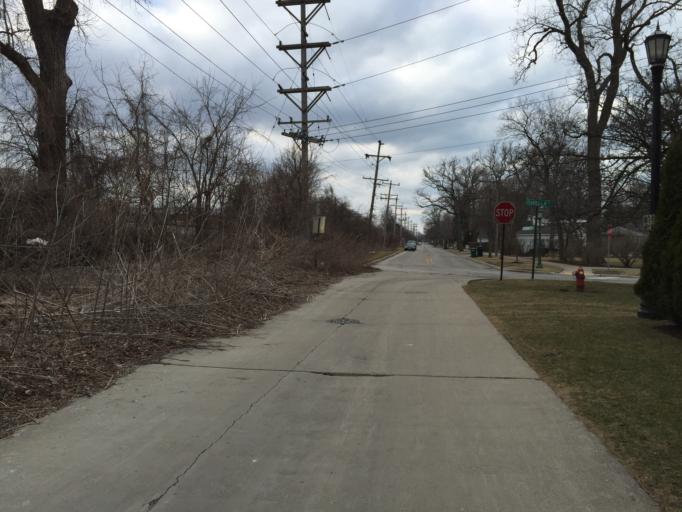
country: US
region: Illinois
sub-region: Cook County
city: Wilmette
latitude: 42.0687
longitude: -87.7018
